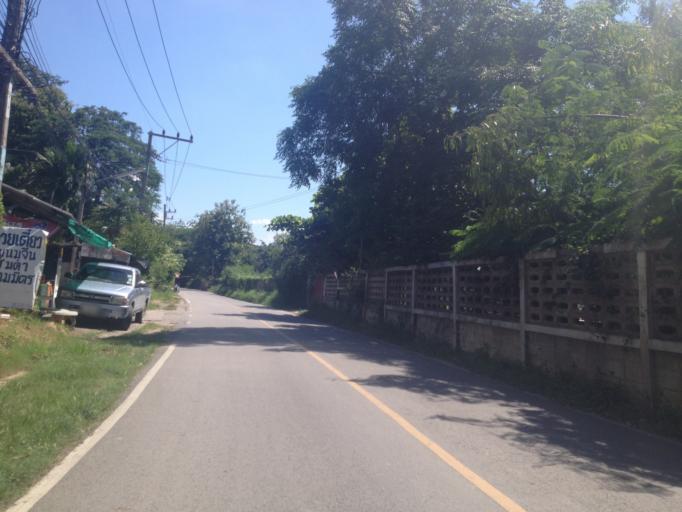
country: TH
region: Chiang Mai
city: Chiang Mai
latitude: 18.7515
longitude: 98.9352
